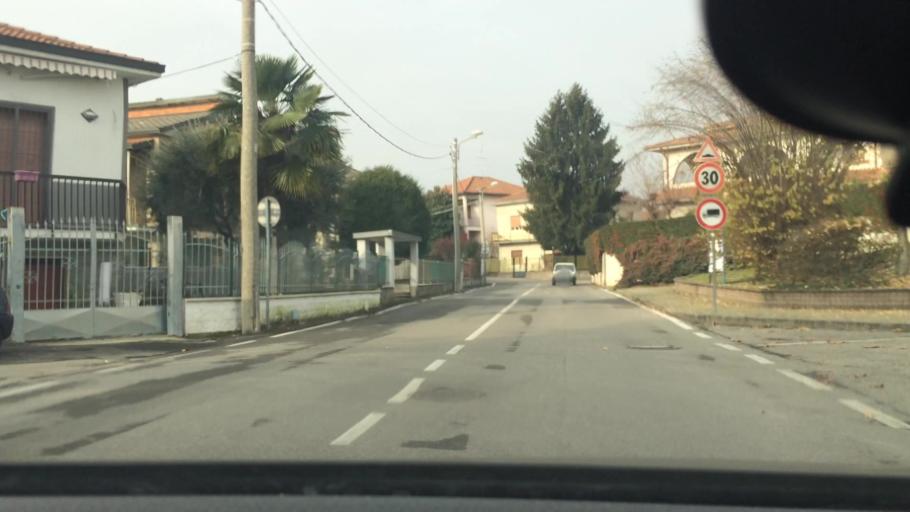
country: IT
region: Lombardy
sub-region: Provincia di Monza e Brianza
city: Villaggio del Sole
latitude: 45.6228
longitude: 9.1064
